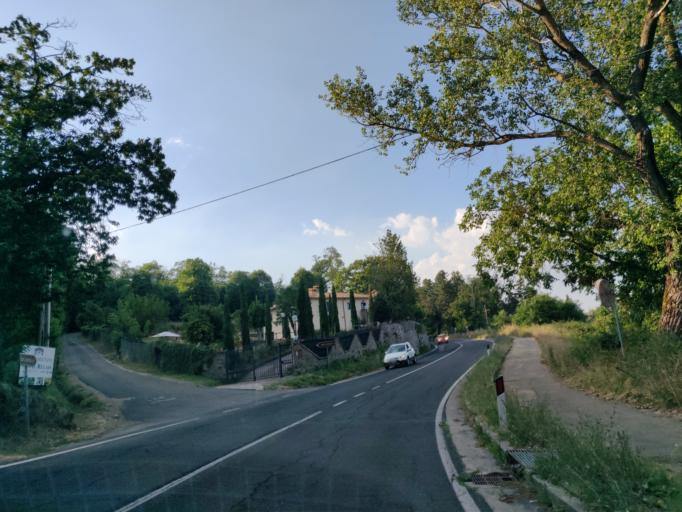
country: IT
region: Tuscany
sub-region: Provincia di Siena
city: Piancastagnaio
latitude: 42.8577
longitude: 11.6837
